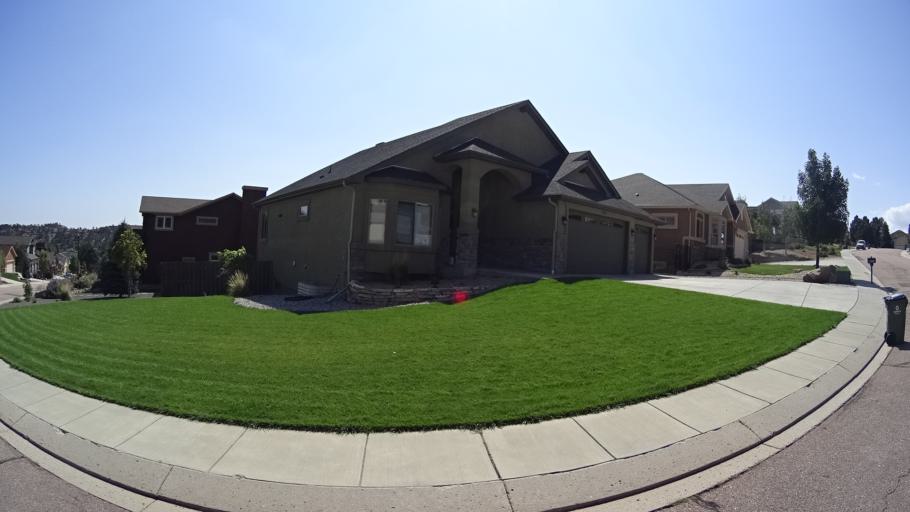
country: US
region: Colorado
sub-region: El Paso County
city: Air Force Academy
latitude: 38.9243
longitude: -104.8703
